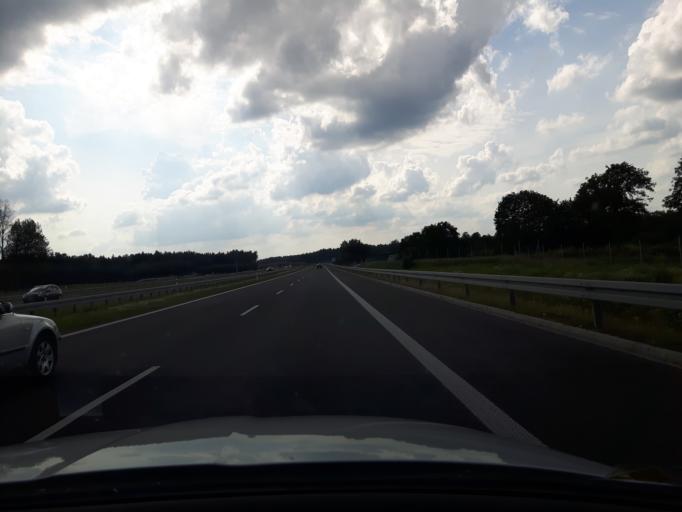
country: PL
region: Warmian-Masurian Voivodeship
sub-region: Powiat olsztynski
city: Olsztynek
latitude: 53.5883
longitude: 20.2244
